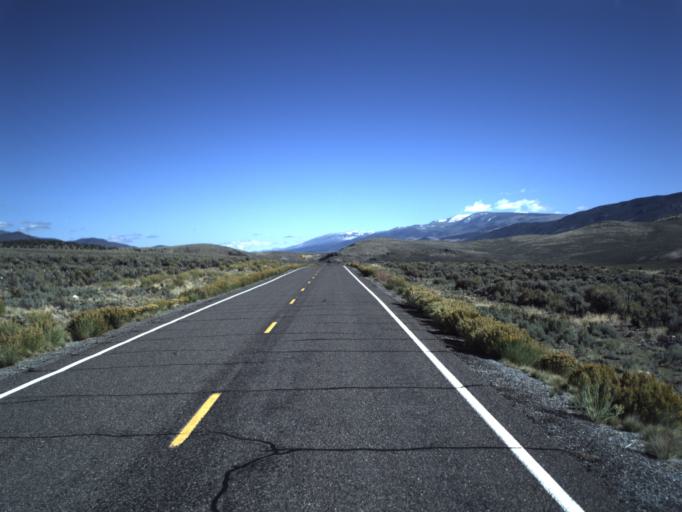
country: US
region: Utah
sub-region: Piute County
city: Junction
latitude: 38.3328
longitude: -111.9569
